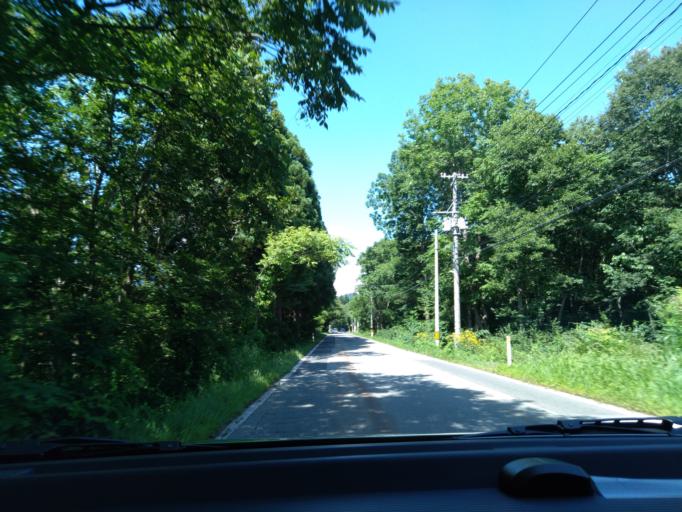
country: JP
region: Akita
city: Kakunodatemachi
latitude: 39.7502
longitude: 140.7243
